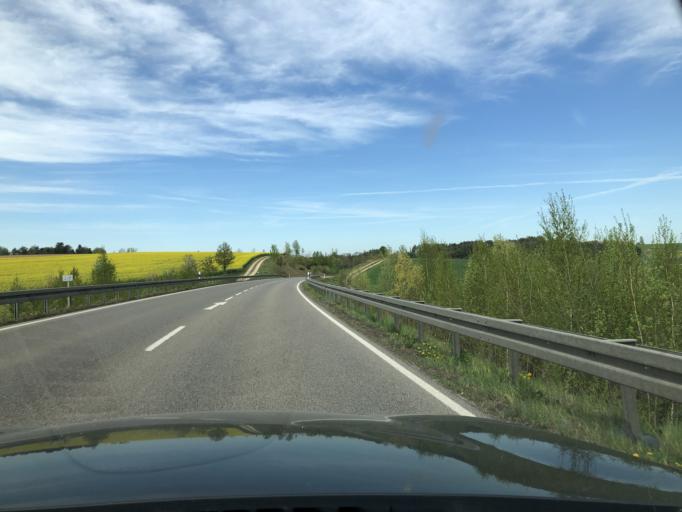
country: DE
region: Bavaria
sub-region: Swabia
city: Laugna
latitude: 48.5485
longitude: 10.7108
